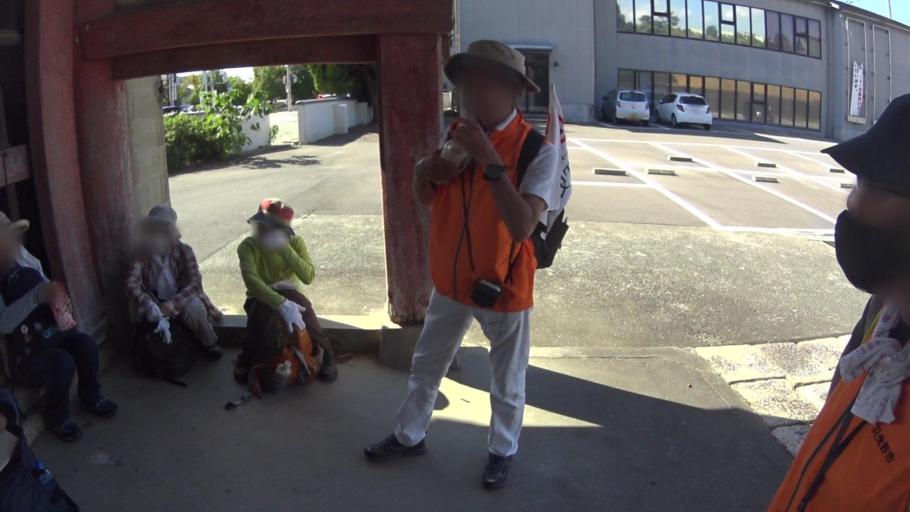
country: JP
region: Ehime
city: Kihoku-cho
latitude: 33.3791
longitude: 132.8174
